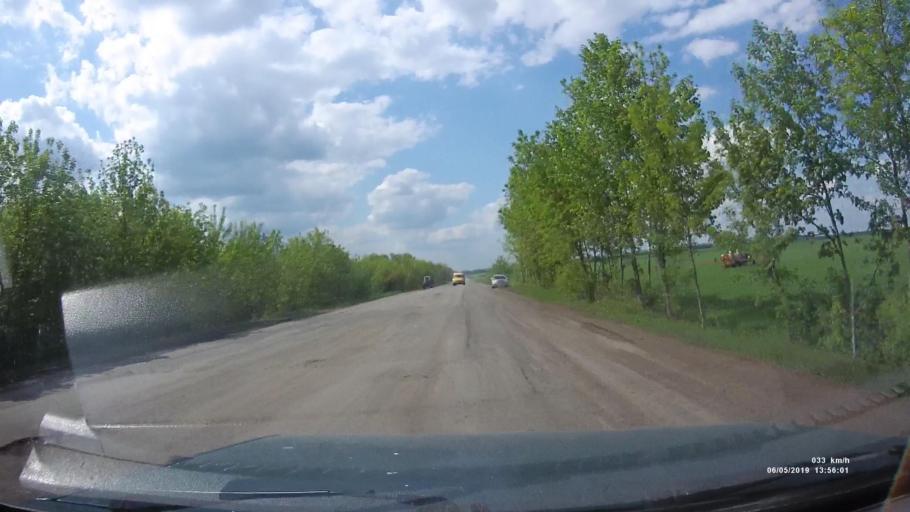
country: RU
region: Rostov
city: Melikhovskaya
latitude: 47.6797
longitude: 40.4345
